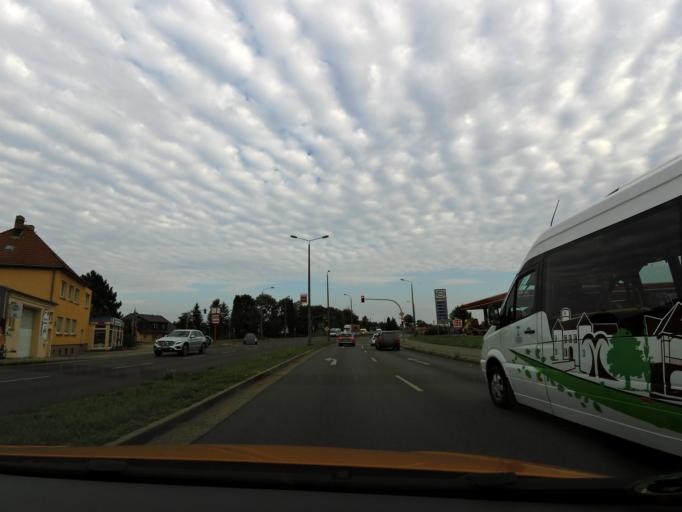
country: DE
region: Brandenburg
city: Brandenburg an der Havel
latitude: 52.4021
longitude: 12.5898
